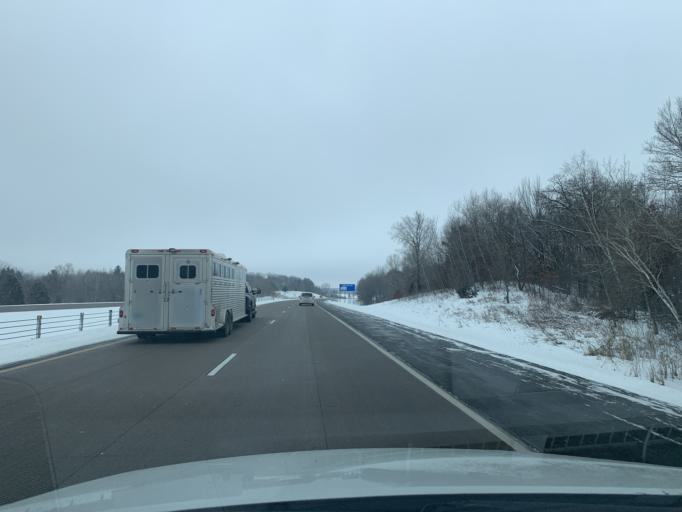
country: US
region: Minnesota
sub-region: Chisago County
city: Harris
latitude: 45.5866
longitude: -92.9940
